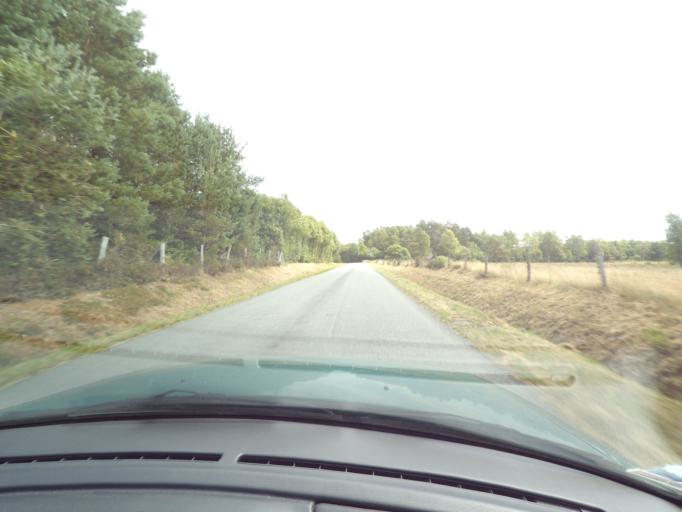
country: FR
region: Limousin
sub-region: Departement de la Correze
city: Bugeat
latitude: 45.7041
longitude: 2.0334
